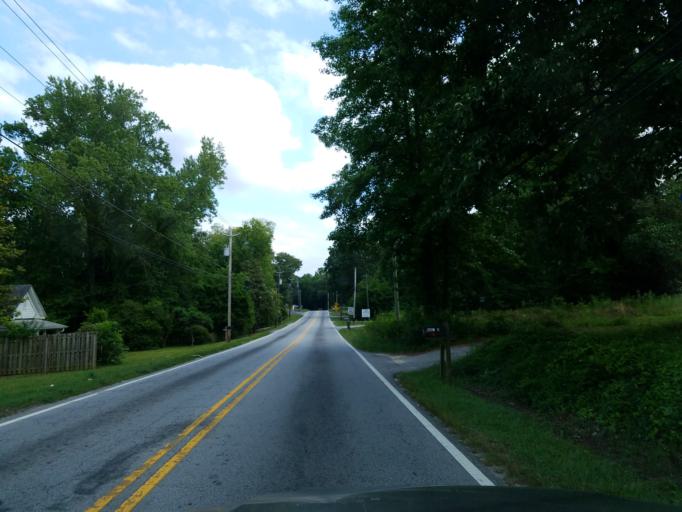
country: US
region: Georgia
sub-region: Douglas County
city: Lithia Springs
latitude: 33.7928
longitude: -84.6603
